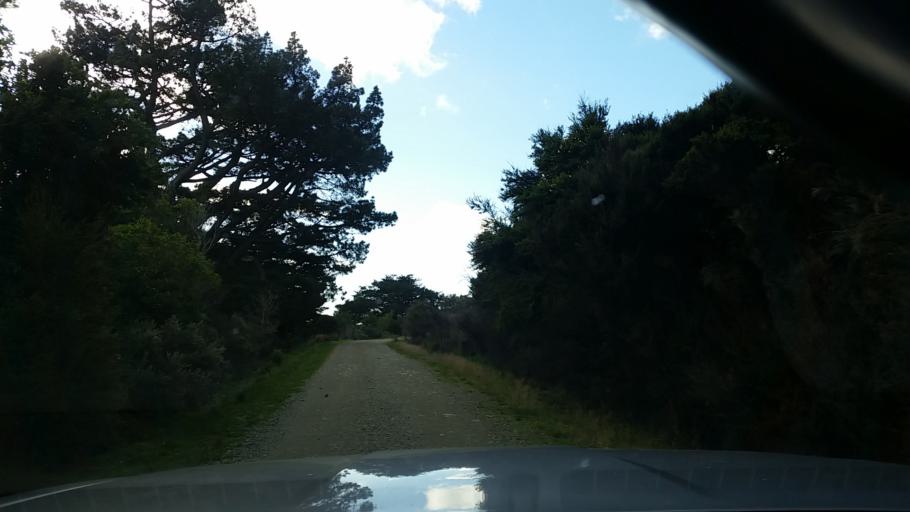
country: NZ
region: Marlborough
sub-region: Marlborough District
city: Picton
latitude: -41.0546
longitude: 174.1098
